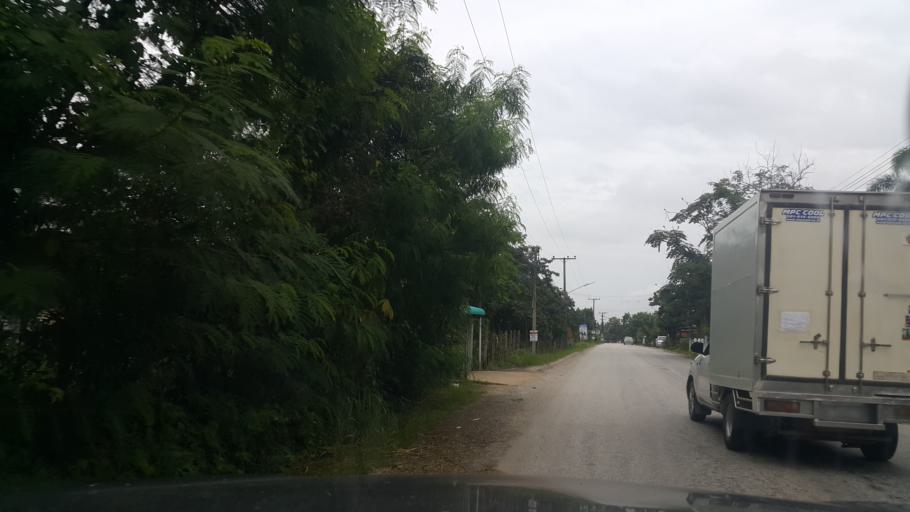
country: TH
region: Chiang Mai
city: San Sai
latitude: 18.9085
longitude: 99.0170
